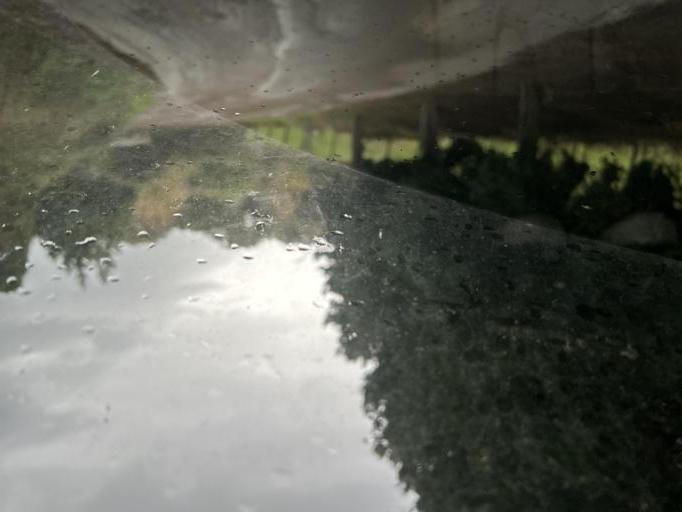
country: IT
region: Calabria
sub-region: Provincia di Catanzaro
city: Staletti
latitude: 38.7659
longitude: 16.5462
